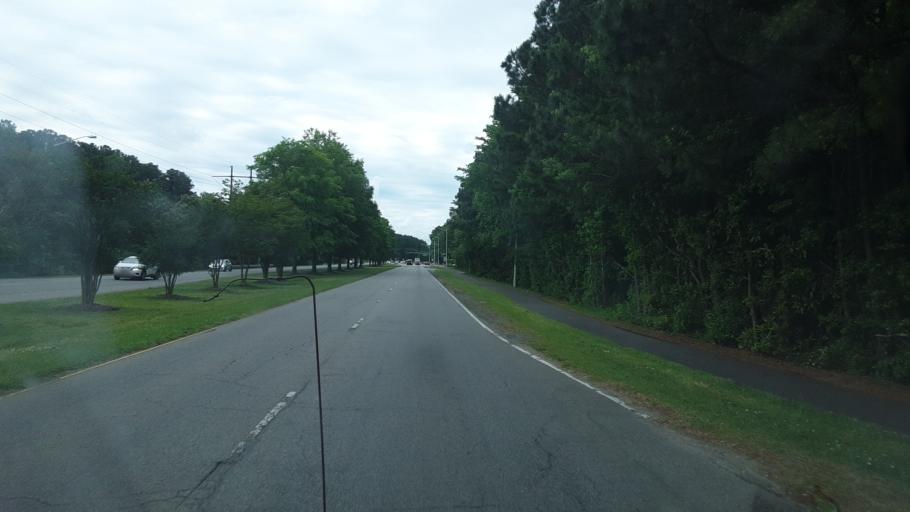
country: US
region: Virginia
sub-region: City of Virginia Beach
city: Virginia Beach
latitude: 36.7973
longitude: -75.9944
